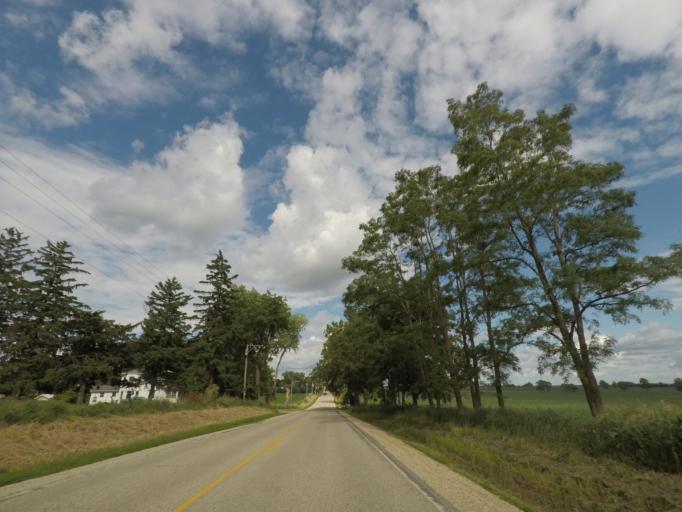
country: US
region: Wisconsin
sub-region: Rock County
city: Orfordville
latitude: 42.7141
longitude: -89.2244
